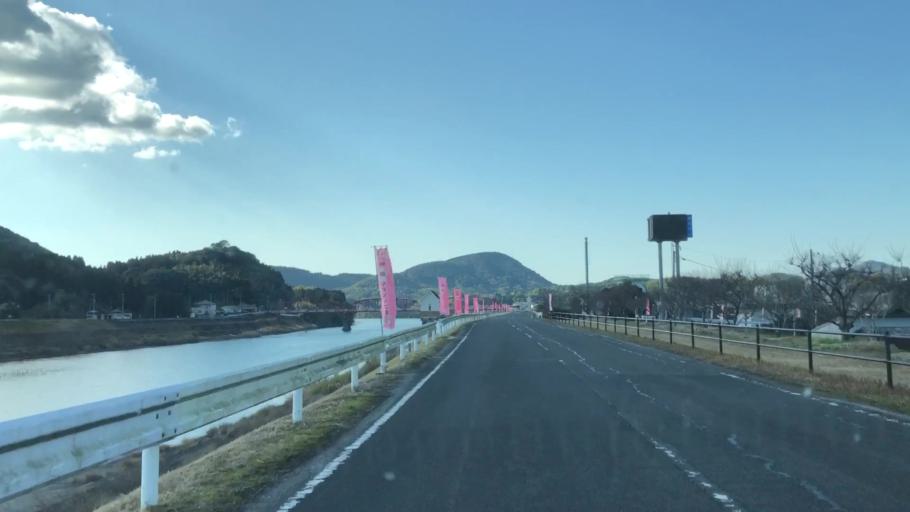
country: JP
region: Kagoshima
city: Satsumasendai
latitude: 31.8609
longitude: 130.3421
